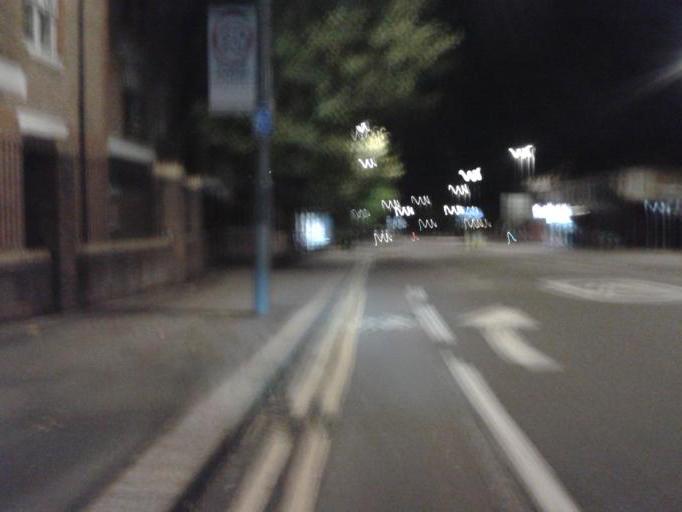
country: GB
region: England
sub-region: Greater London
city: Walthamstow
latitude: 51.5903
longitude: -0.0180
